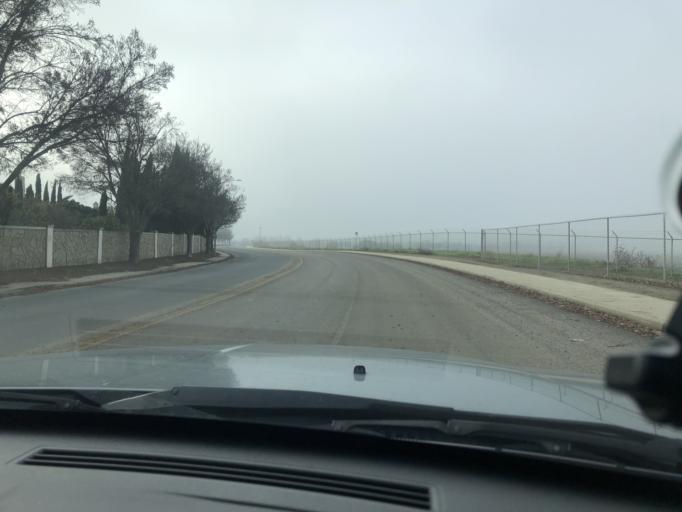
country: US
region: California
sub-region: Monterey County
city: King City
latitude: 36.2148
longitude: -121.1399
